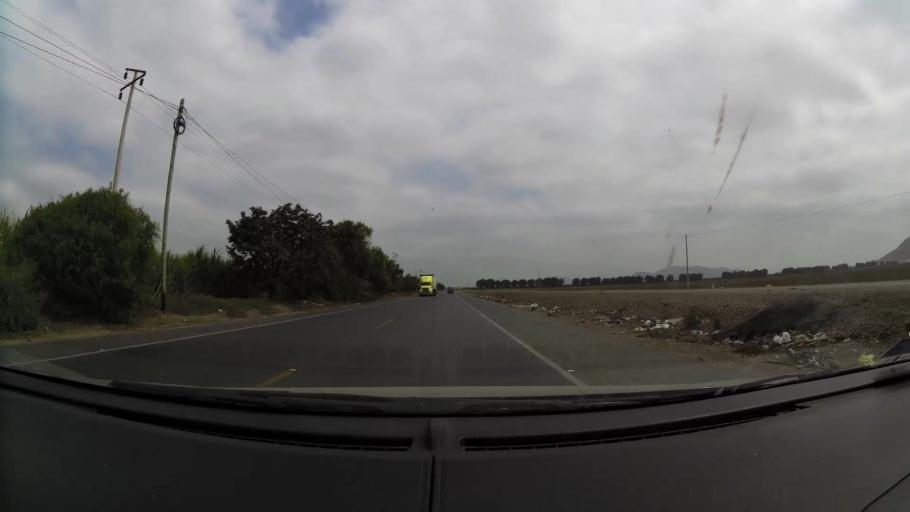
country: PE
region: La Libertad
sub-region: Ascope
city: Chocope
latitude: -7.8017
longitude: -79.1982
